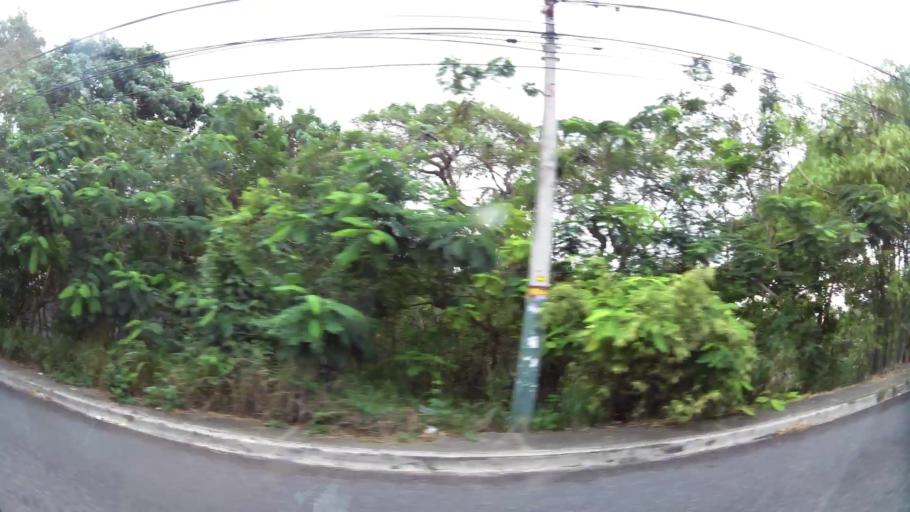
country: DO
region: Nacional
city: La Agustina
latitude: 18.5085
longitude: -69.9494
